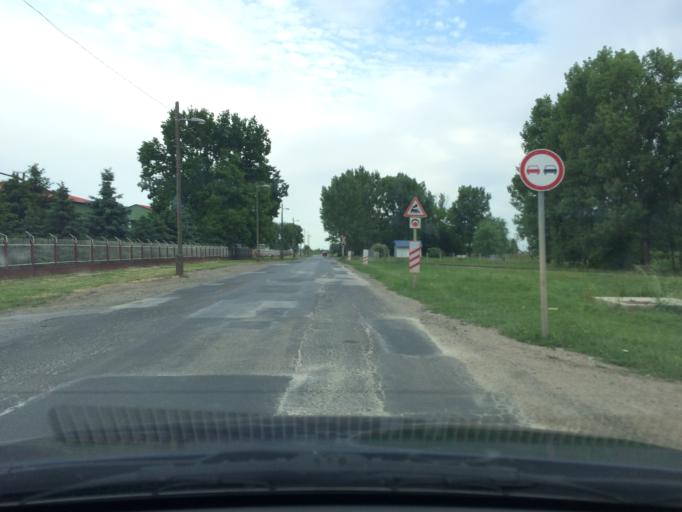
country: HU
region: Hajdu-Bihar
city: Hajdunanas
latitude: 47.9061
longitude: 21.4037
